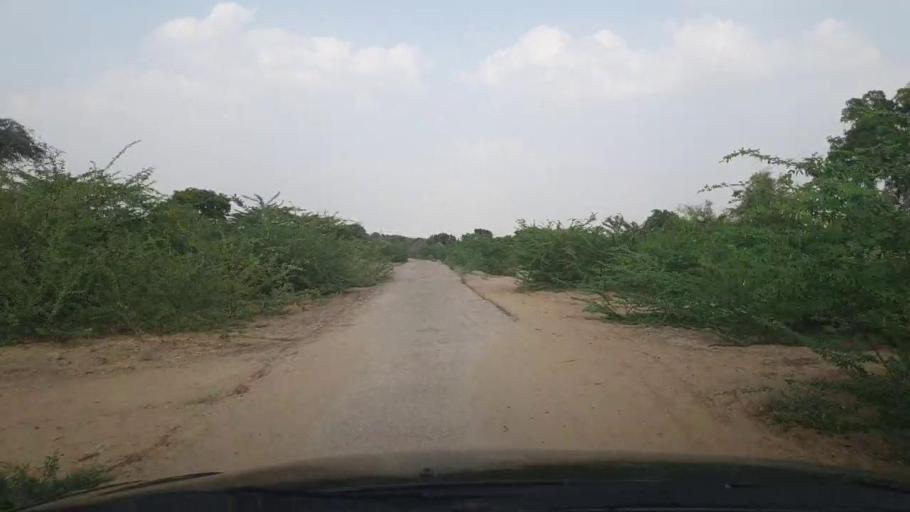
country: PK
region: Sindh
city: Islamkot
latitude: 24.9882
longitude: 70.5766
